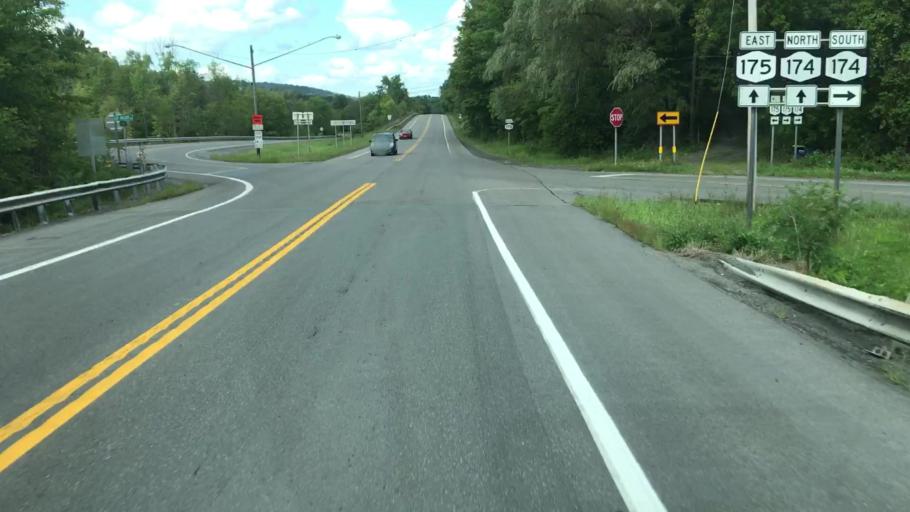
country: US
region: New York
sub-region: Onondaga County
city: Marcellus
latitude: 42.9628
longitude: -76.3355
